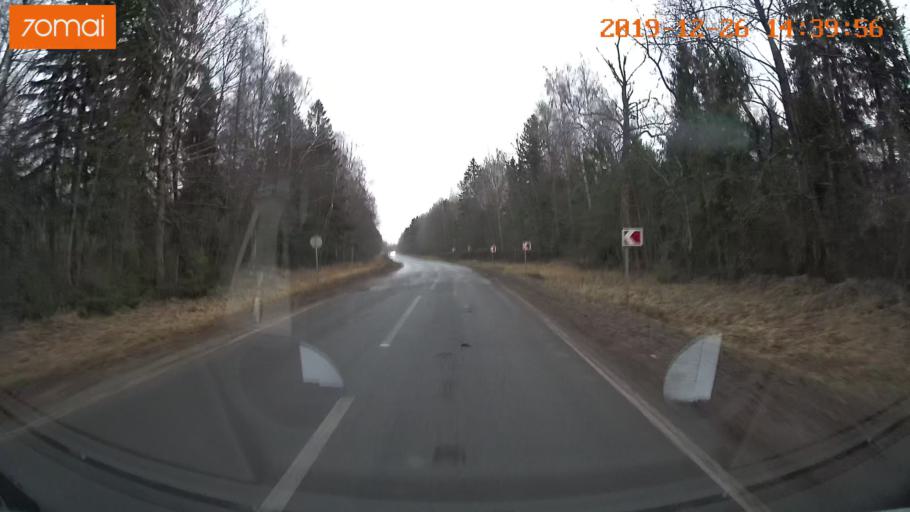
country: RU
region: Jaroslavl
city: Poshekhon'ye
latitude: 58.3790
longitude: 38.9883
